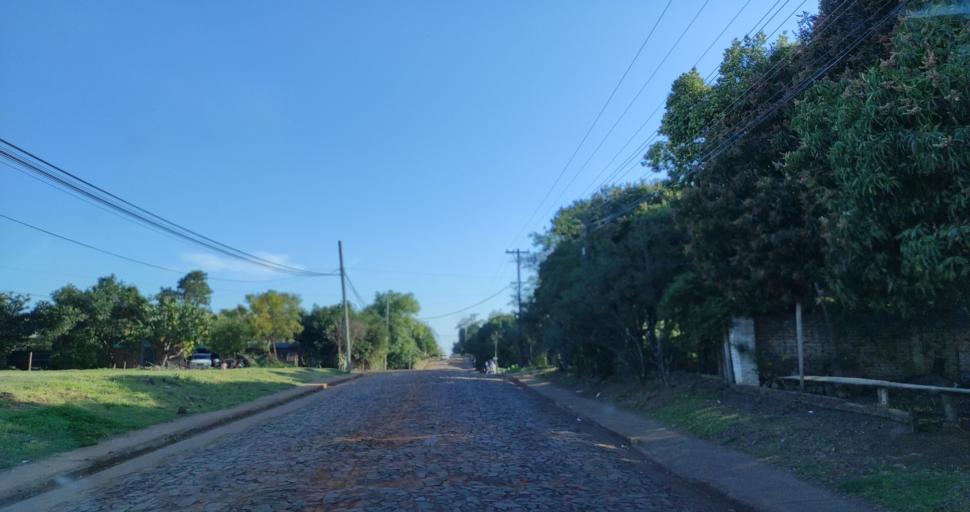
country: AR
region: Misiones
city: Garupa
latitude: -27.4486
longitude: -55.8611
